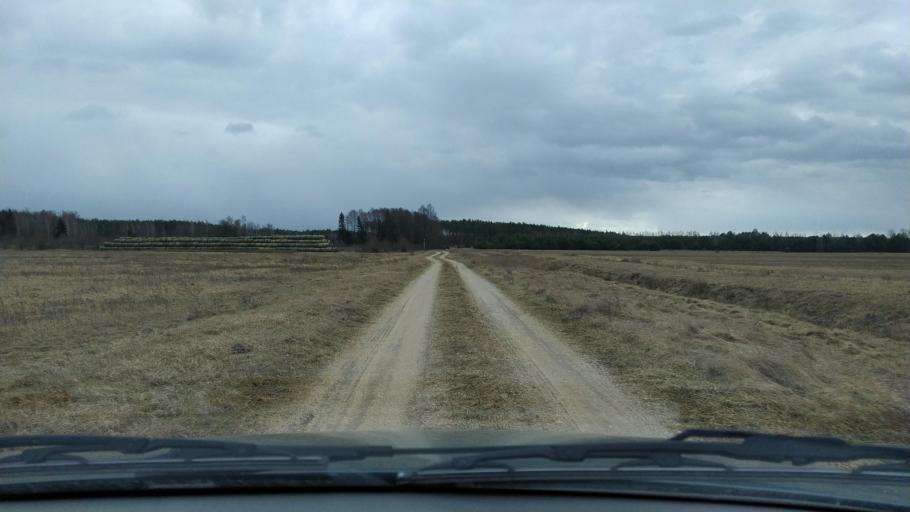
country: BY
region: Brest
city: Zhabinka
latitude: 52.4078
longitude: 24.0683
